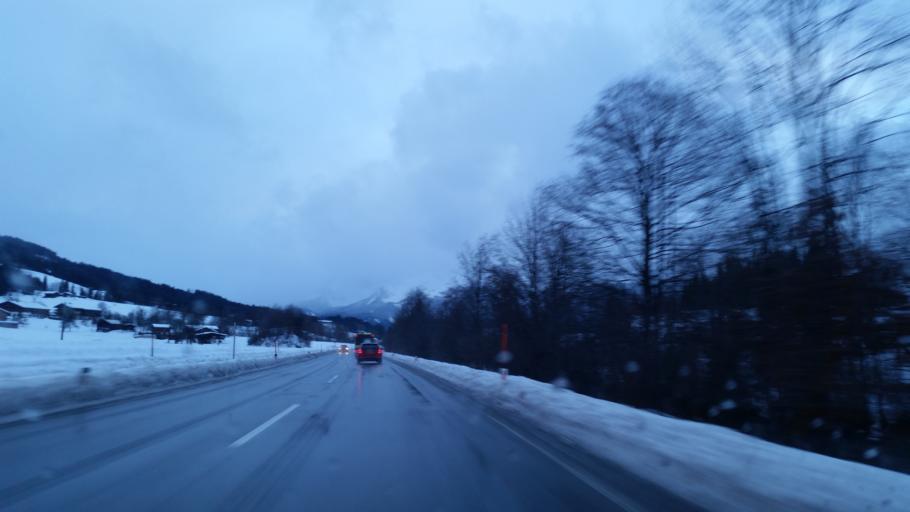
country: AT
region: Tyrol
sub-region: Politischer Bezirk Kitzbuhel
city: Sankt Johann in Tirol
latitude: 47.5049
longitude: 12.4773
